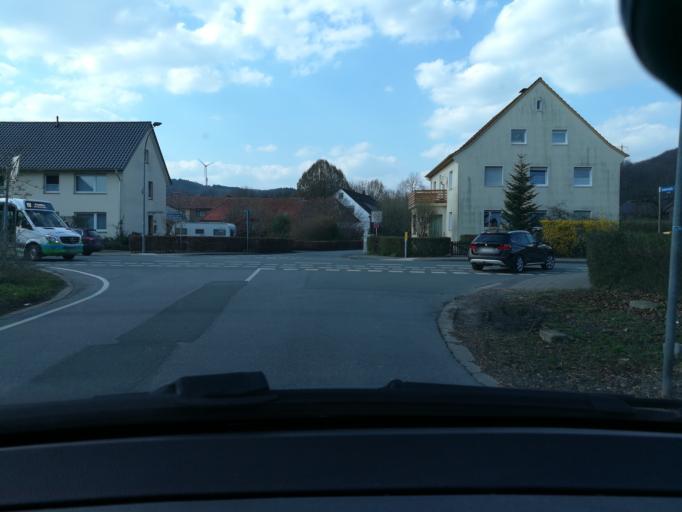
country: DE
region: North Rhine-Westphalia
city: Borgholzhausen
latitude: 52.1065
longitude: 8.3076
